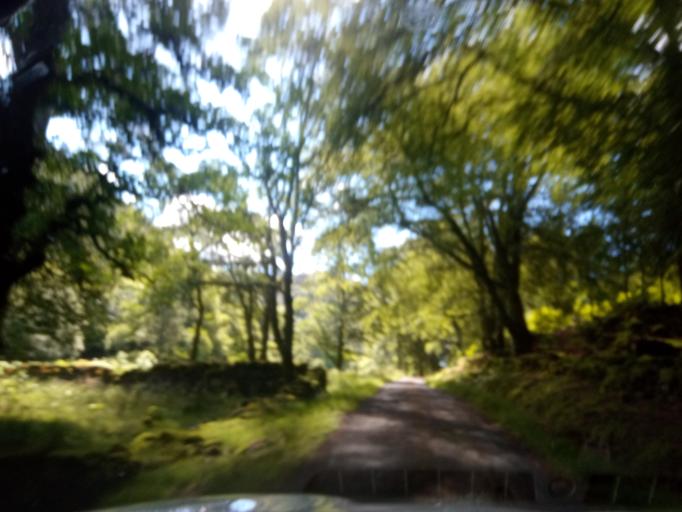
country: GB
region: Scotland
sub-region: Argyll and Bute
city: Isle Of Mull
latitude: 56.7785
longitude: -5.8249
